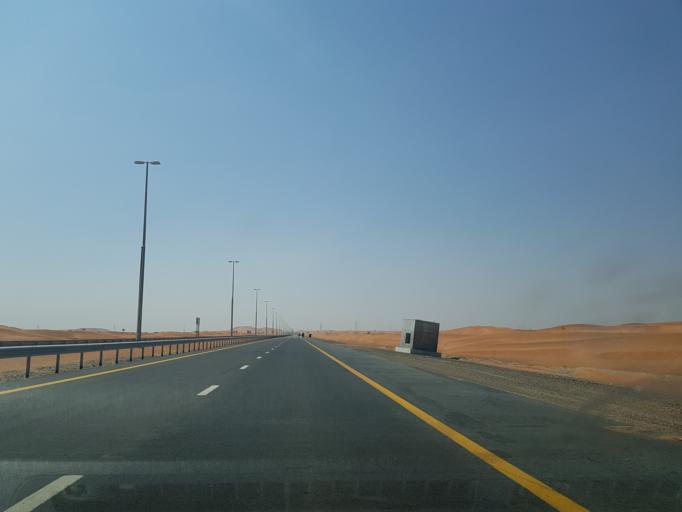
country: AE
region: Ash Shariqah
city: Adh Dhayd
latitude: 25.2408
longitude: 55.8821
